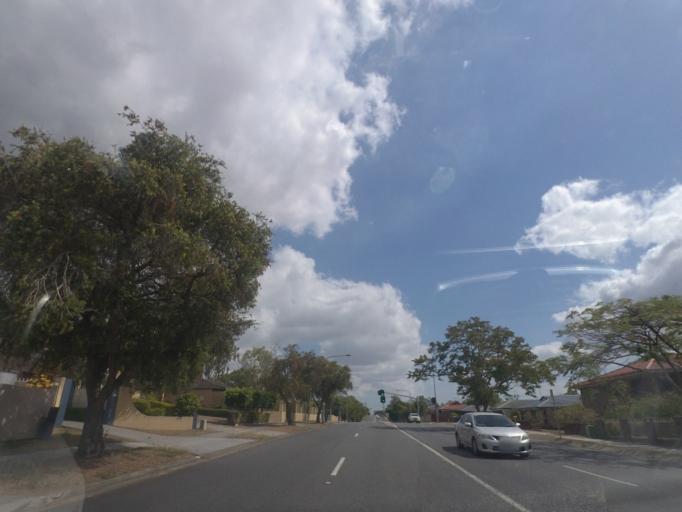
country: AU
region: Queensland
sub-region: Brisbane
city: Upper Mount Gravatt
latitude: -27.5643
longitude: 153.0884
